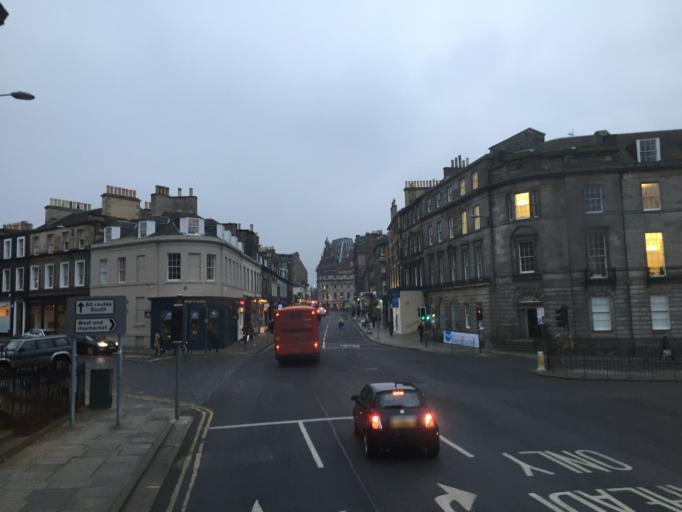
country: GB
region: Scotland
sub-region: Edinburgh
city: Edinburgh
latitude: 55.9514
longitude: -3.2110
